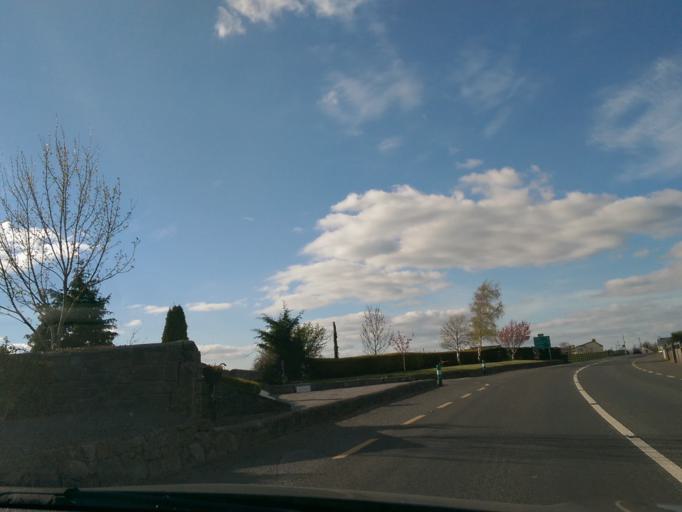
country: IE
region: Connaught
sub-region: County Galway
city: Portumna
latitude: 53.1021
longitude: -8.2333
